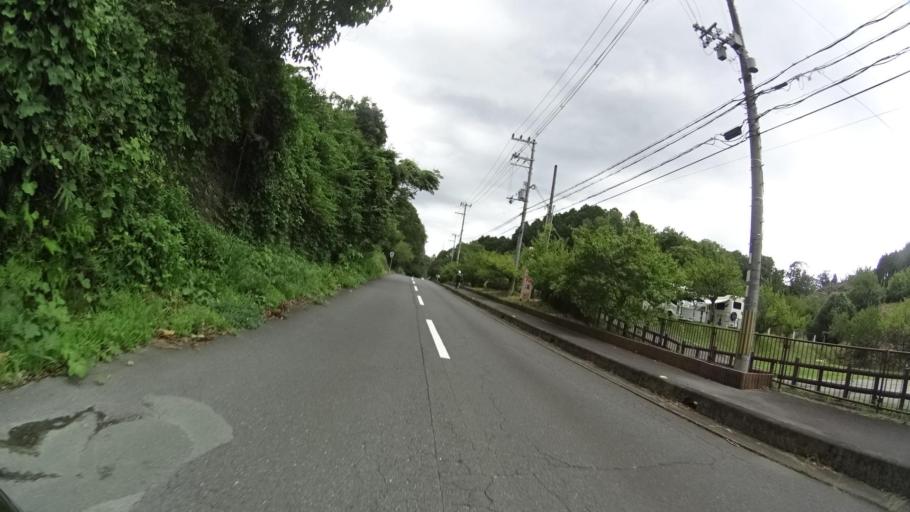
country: JP
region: Mie
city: Ueno-ebisumachi
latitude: 34.7122
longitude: 136.0351
